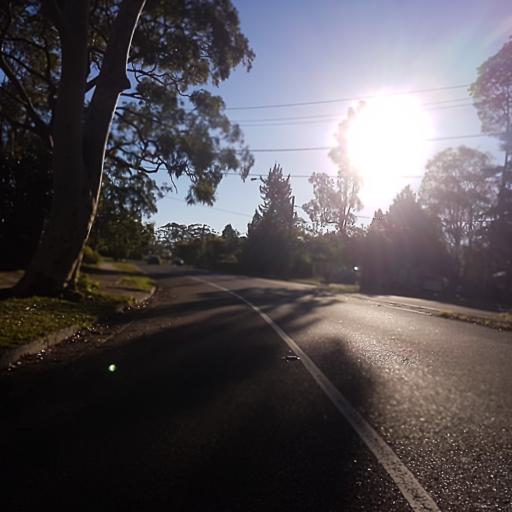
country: AU
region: New South Wales
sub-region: Warringah
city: Davidson
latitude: -33.7409
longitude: 151.2089
